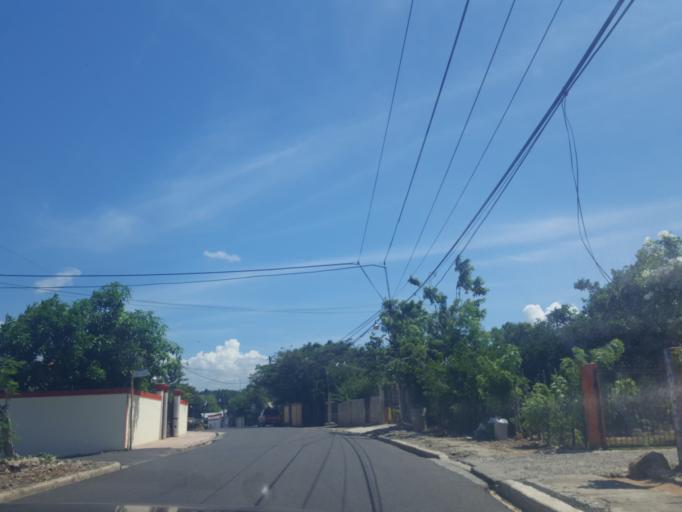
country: DO
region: Santiago
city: Licey al Medio
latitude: 19.3928
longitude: -70.6480
